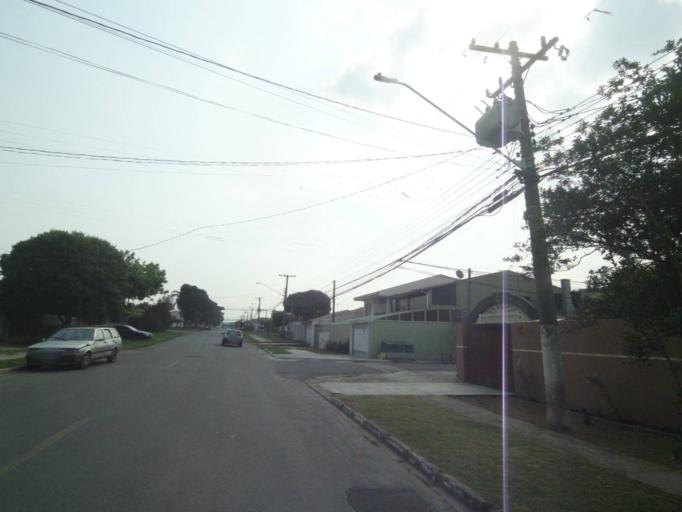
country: BR
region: Parana
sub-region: Sao Jose Dos Pinhais
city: Sao Jose dos Pinhais
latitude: -25.5272
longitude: -49.2313
